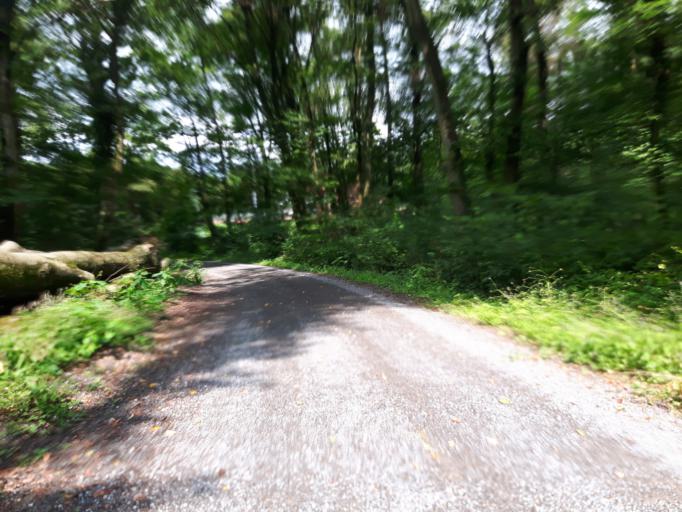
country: DE
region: Baden-Wuerttemberg
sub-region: Regierungsbezirk Stuttgart
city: Eppingen
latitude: 49.1296
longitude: 8.9342
